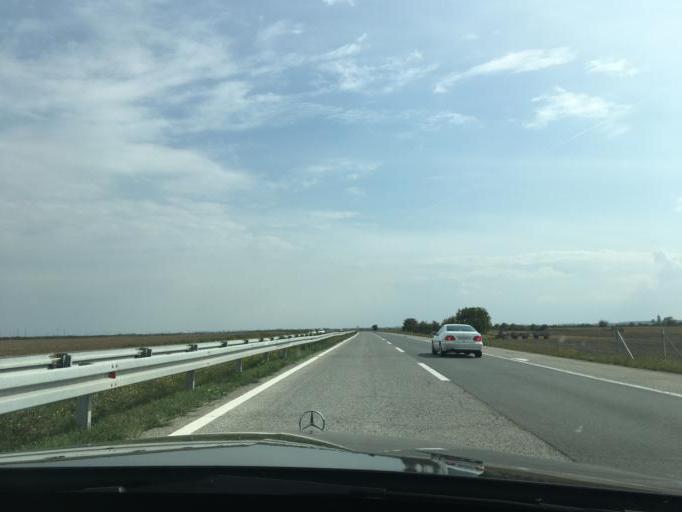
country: RS
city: Ravnje
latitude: 45.0248
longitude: 19.4840
